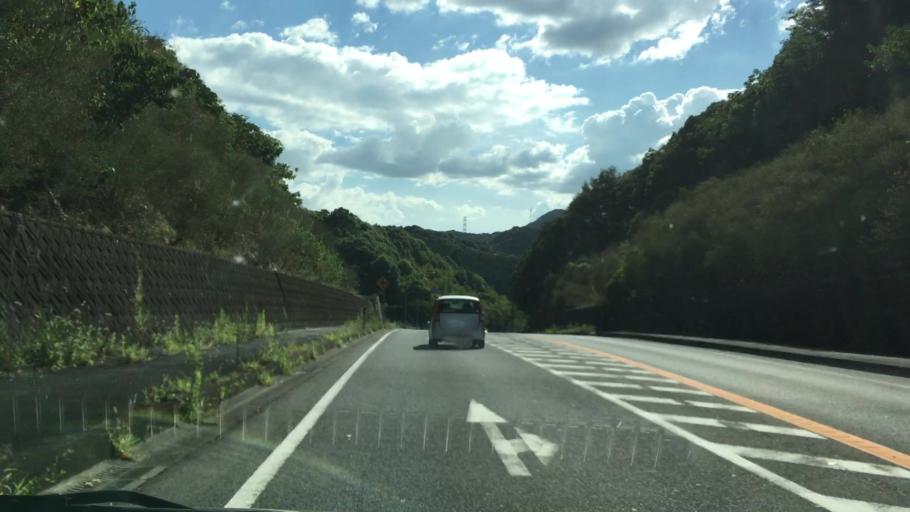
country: JP
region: Saga Prefecture
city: Takeocho-takeo
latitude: 33.1889
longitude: 129.9330
